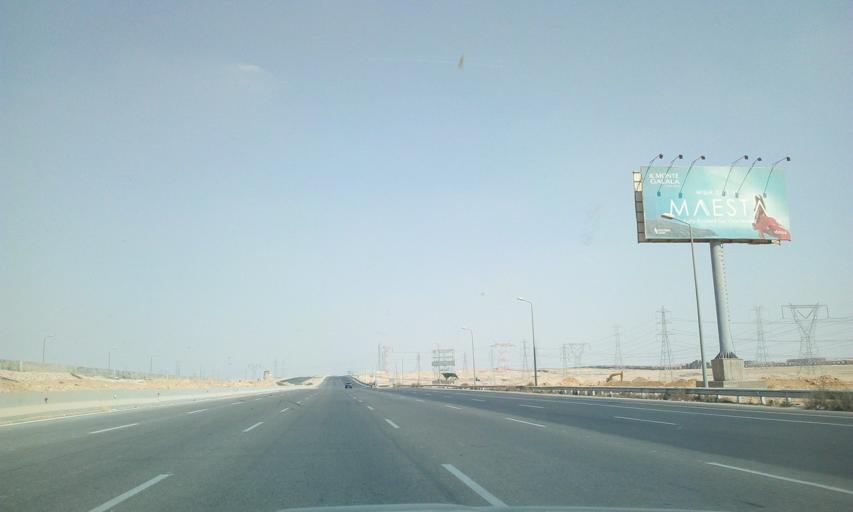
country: EG
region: Muhafazat al Qahirah
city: Halwan
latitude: 29.9065
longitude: 31.6703
